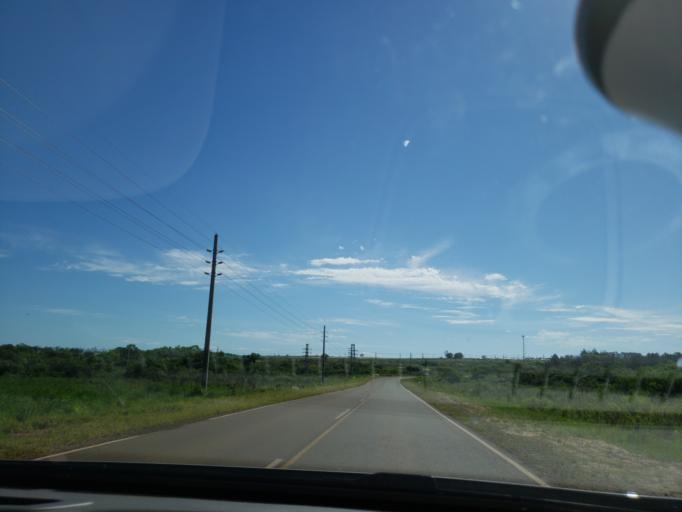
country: AR
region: Misiones
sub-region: Departamento de Capital
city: Posadas
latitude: -27.3898
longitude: -55.9831
